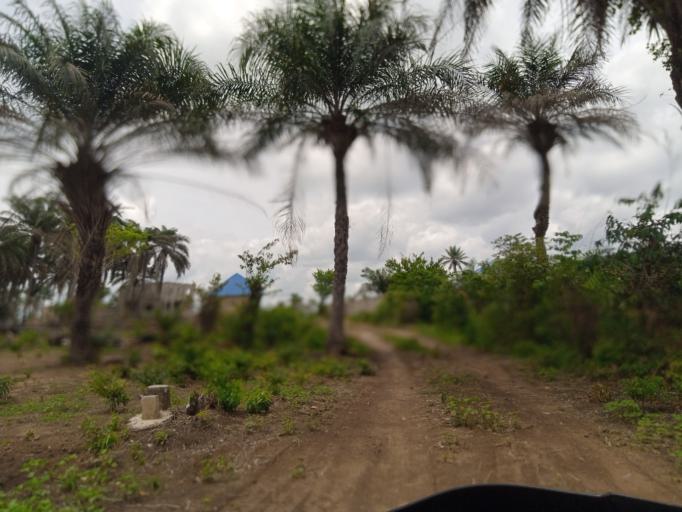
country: SL
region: Western Area
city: Waterloo
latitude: 8.3279
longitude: -13.0019
